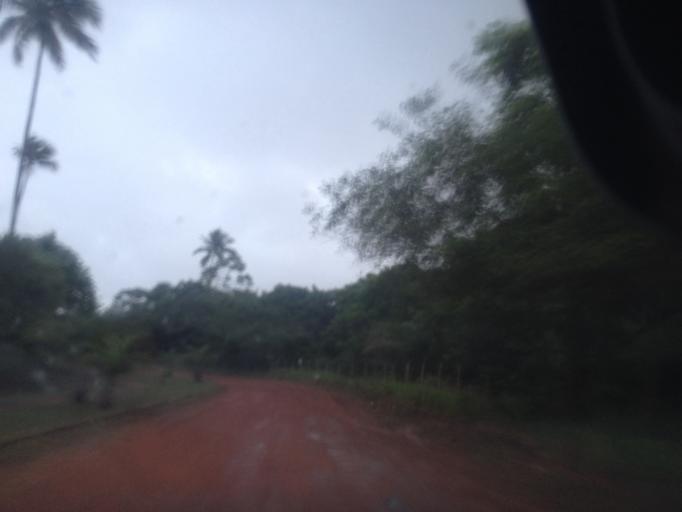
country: BR
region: Bahia
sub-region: Mata De Sao Joao
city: Mata de Sao Joao
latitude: -12.5785
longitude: -38.0328
